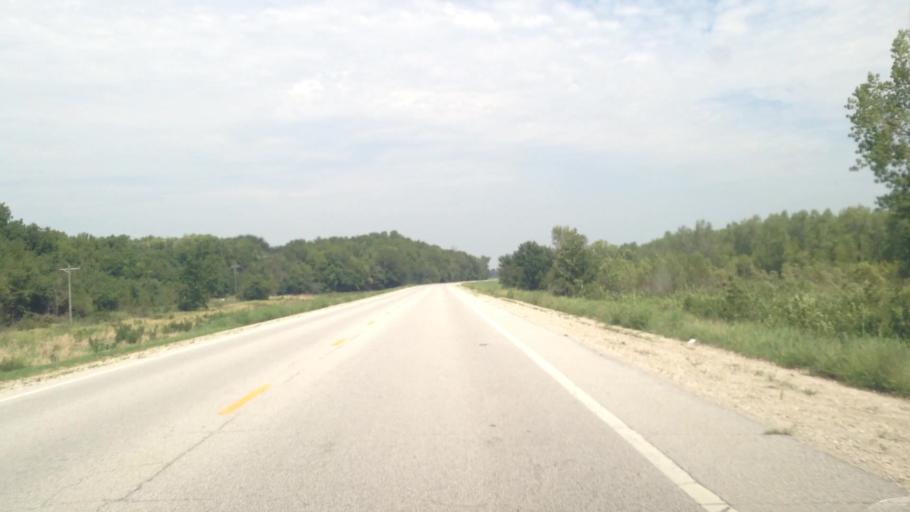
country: US
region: Kansas
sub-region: Neosho County
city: Erie
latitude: 37.5370
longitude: -95.2700
